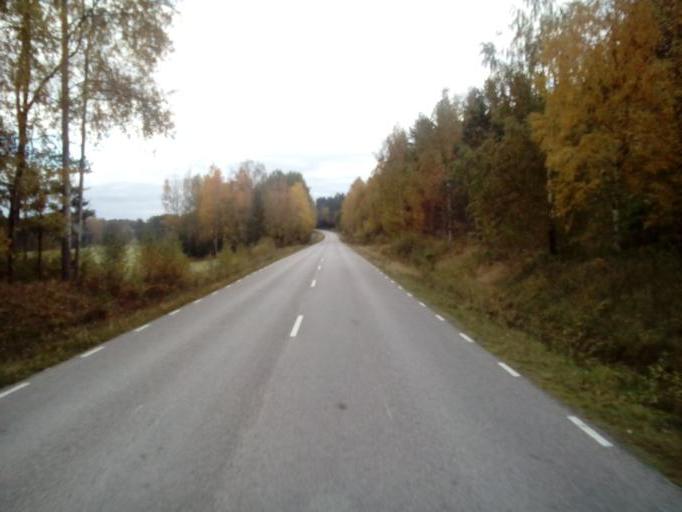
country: SE
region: Kalmar
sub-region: Vasterviks Kommun
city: Gamleby
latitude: 57.8879
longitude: 16.3410
